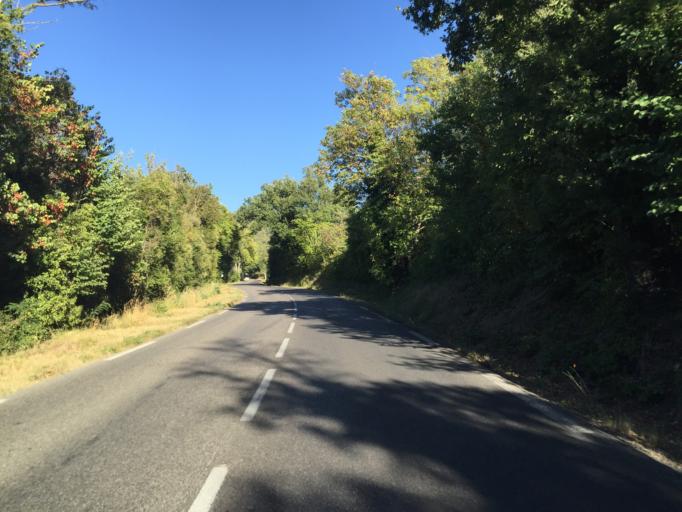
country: FR
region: Provence-Alpes-Cote d'Azur
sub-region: Departement du Vaucluse
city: Saignon
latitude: 43.8800
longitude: 5.4388
